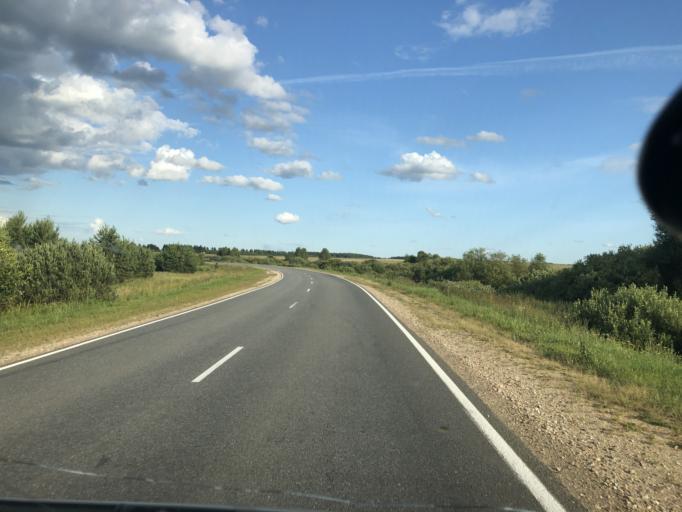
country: RU
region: Kaluga
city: Yukhnov
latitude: 54.7017
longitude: 35.2711
